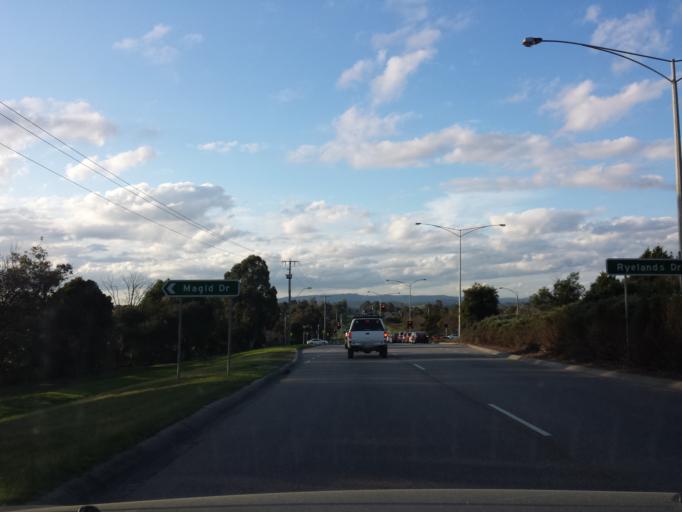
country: AU
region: Victoria
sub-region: Casey
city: Narre Warren
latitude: -38.0151
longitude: 145.3089
